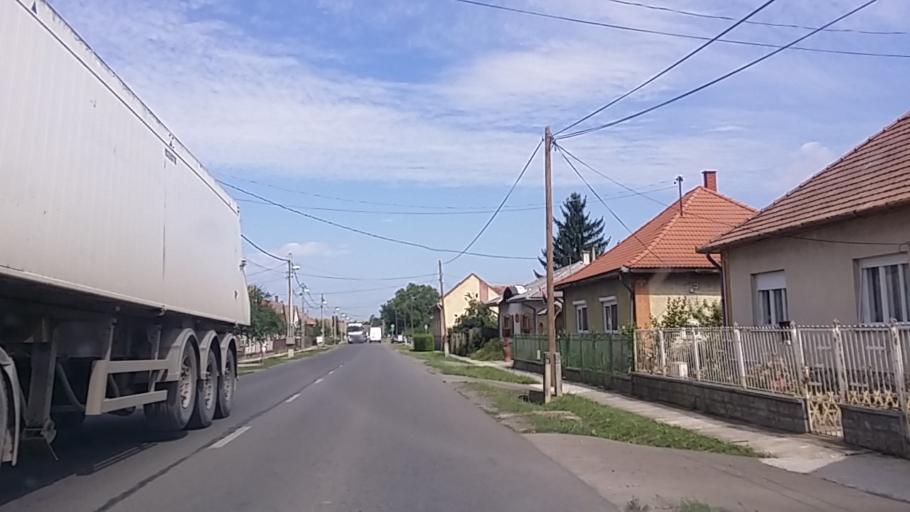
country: HU
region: Tolna
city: Dombovar
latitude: 46.3300
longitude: 18.1282
